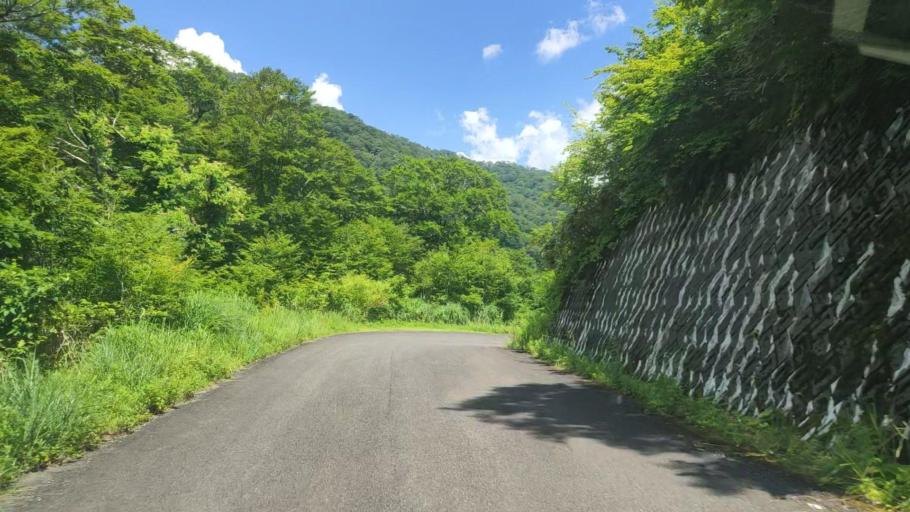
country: JP
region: Fukui
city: Ono
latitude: 35.7779
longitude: 136.5206
